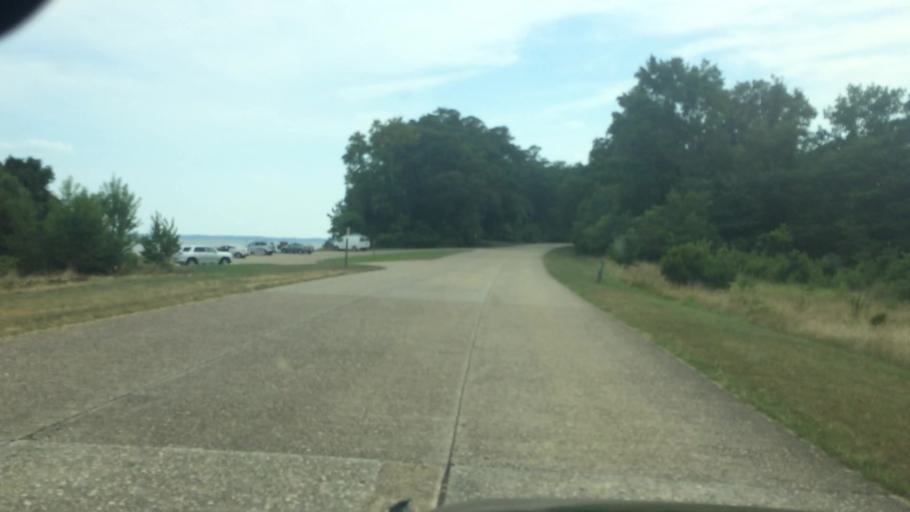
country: US
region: Virginia
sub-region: City of Williamsburg
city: Williamsburg
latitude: 37.2205
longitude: -76.6983
